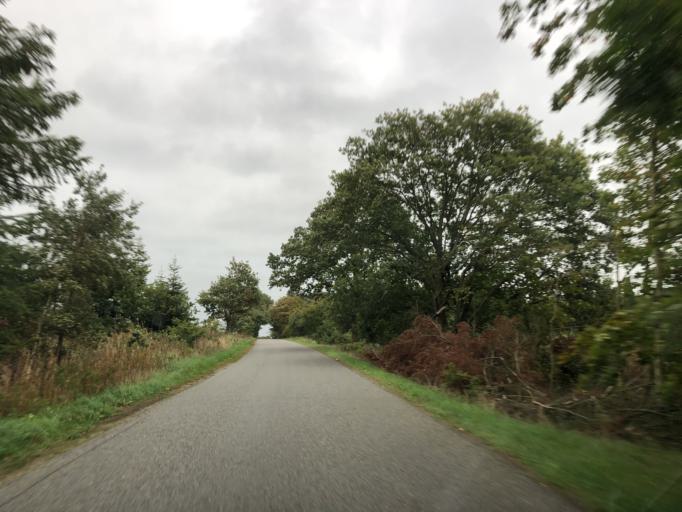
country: DK
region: Central Jutland
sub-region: Viborg Kommune
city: Viborg
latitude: 56.4168
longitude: 9.3049
